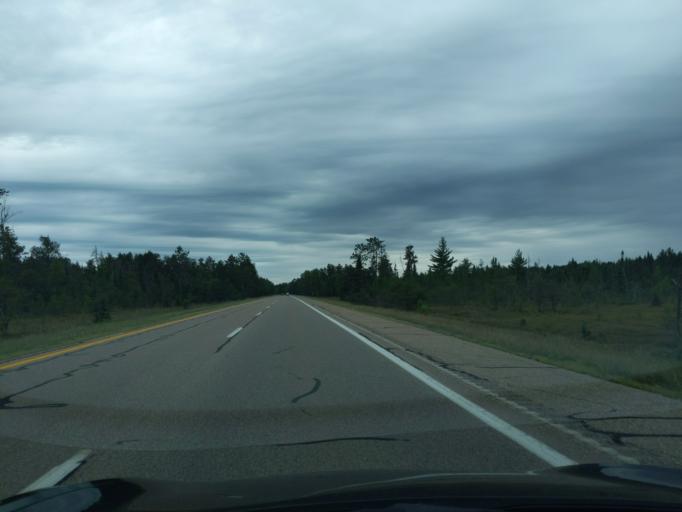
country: US
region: Michigan
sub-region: Roscommon County
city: Houghton Lake
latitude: 44.2443
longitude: -84.8039
